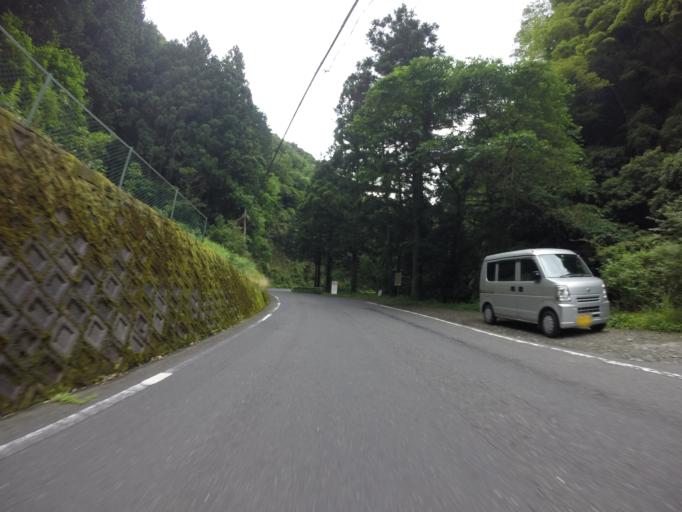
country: JP
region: Shizuoka
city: Shizuoka-shi
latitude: 35.0258
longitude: 138.2886
